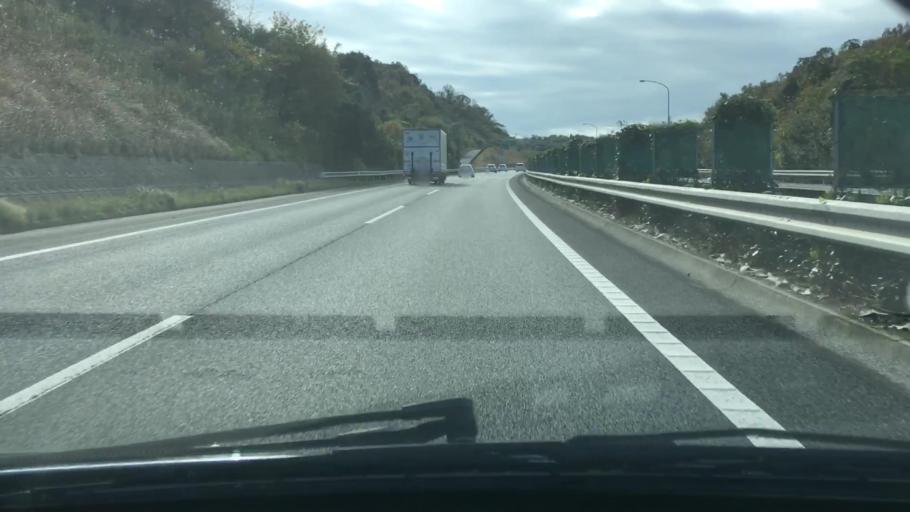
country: JP
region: Chiba
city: Ichihara
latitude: 35.4643
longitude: 140.0858
